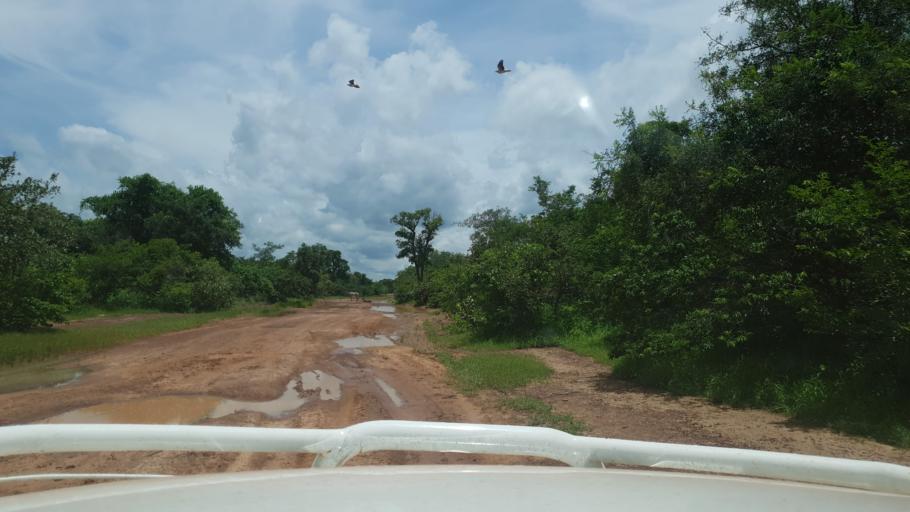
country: ML
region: Koulikoro
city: Banamba
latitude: 13.2009
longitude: -7.3385
